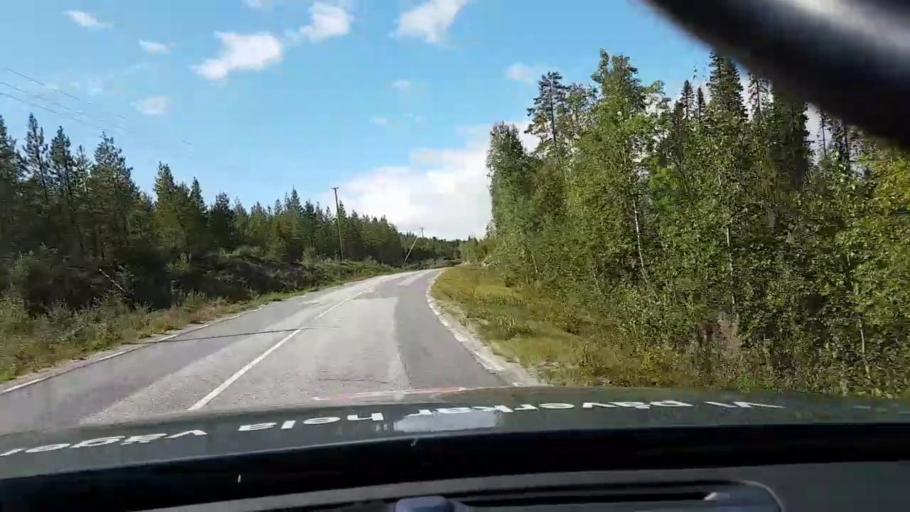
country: SE
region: Vaesterbotten
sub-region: Asele Kommun
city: Asele
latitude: 63.8288
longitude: 17.4625
